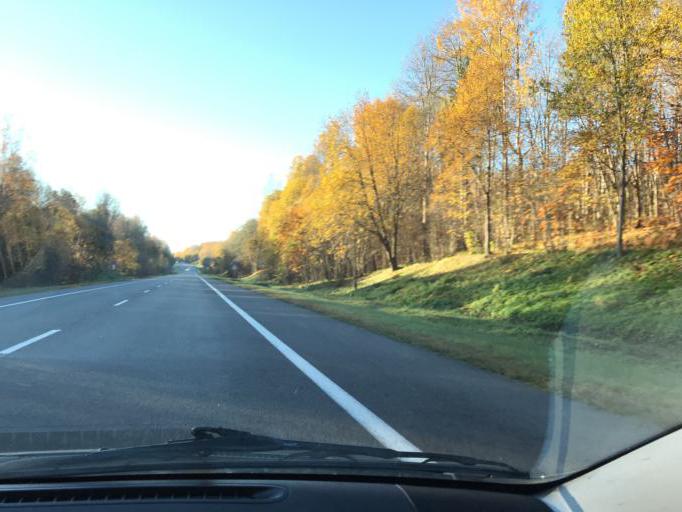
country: BY
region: Vitebsk
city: Vitebsk
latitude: 55.0312
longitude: 30.3228
